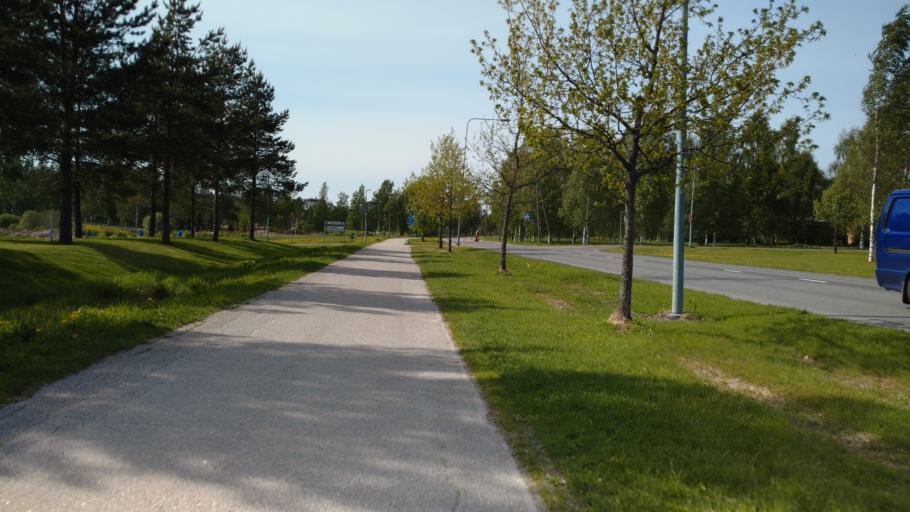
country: FI
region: Varsinais-Suomi
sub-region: Salo
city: Salo
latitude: 60.3799
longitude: 23.1514
